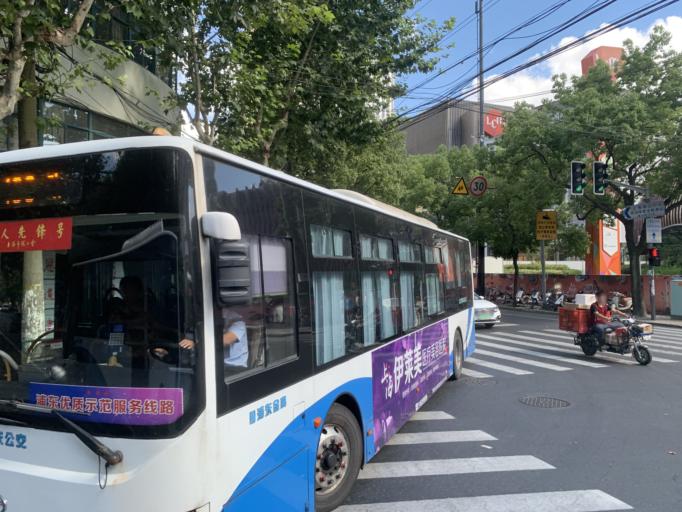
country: CN
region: Shanghai Shi
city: Pudong
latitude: 31.2467
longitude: 121.5512
